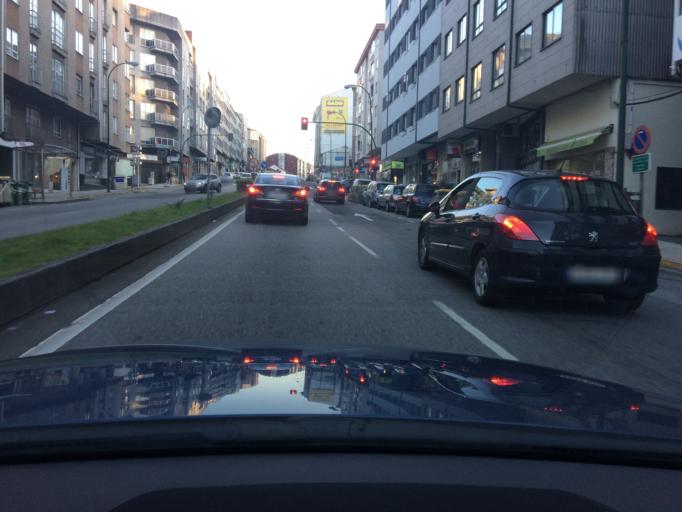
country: ES
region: Galicia
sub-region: Provincia da Coruna
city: Santiago de Compostela
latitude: 42.8454
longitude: -8.5761
